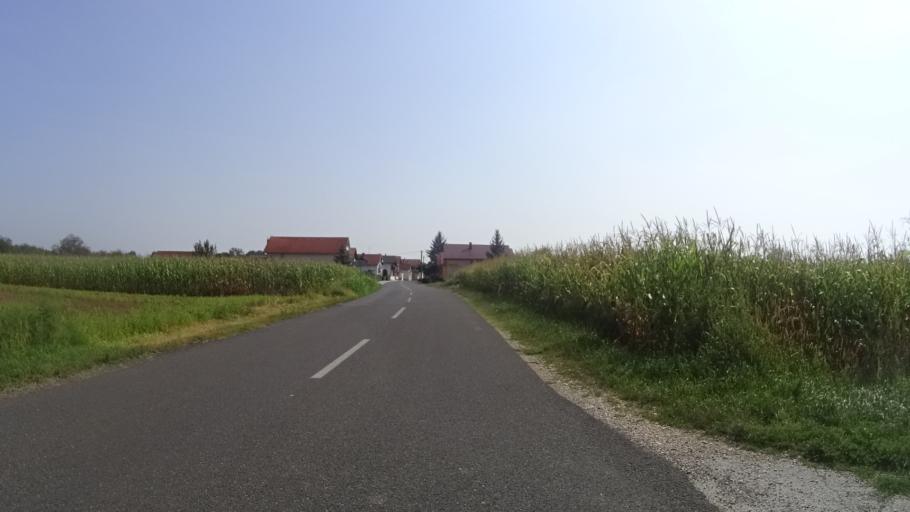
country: HR
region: Medimurska
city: Palovec
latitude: 46.3925
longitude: 16.5840
